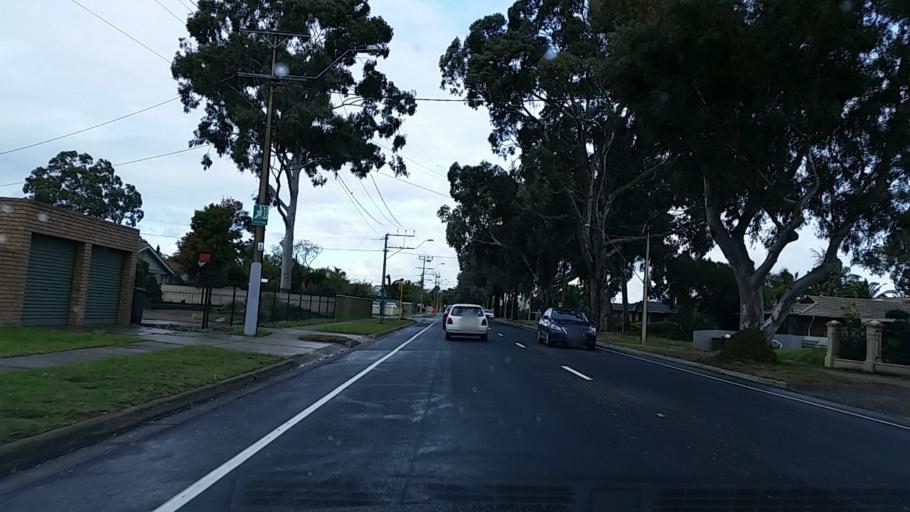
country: AU
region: South Australia
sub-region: Salisbury
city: Salisbury
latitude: -34.7682
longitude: 138.6298
